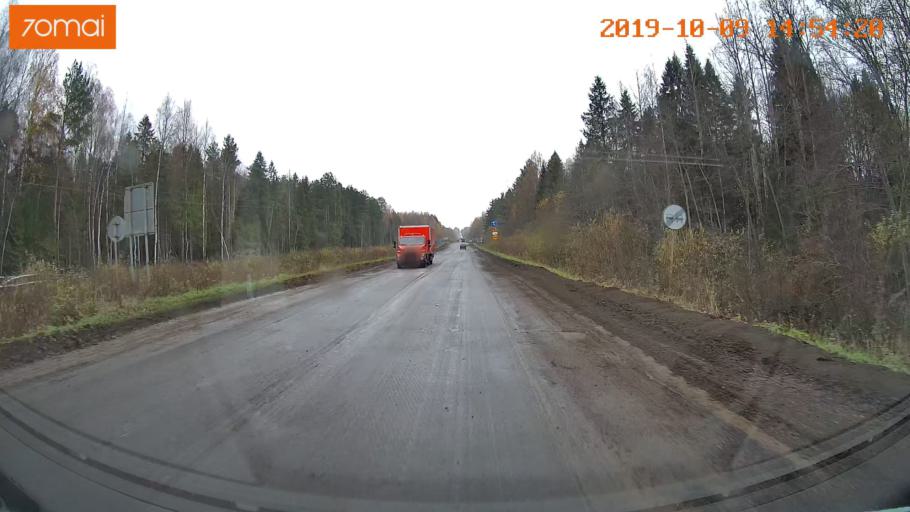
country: RU
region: Kostroma
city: Chistyye Bory
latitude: 58.3576
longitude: 41.6424
